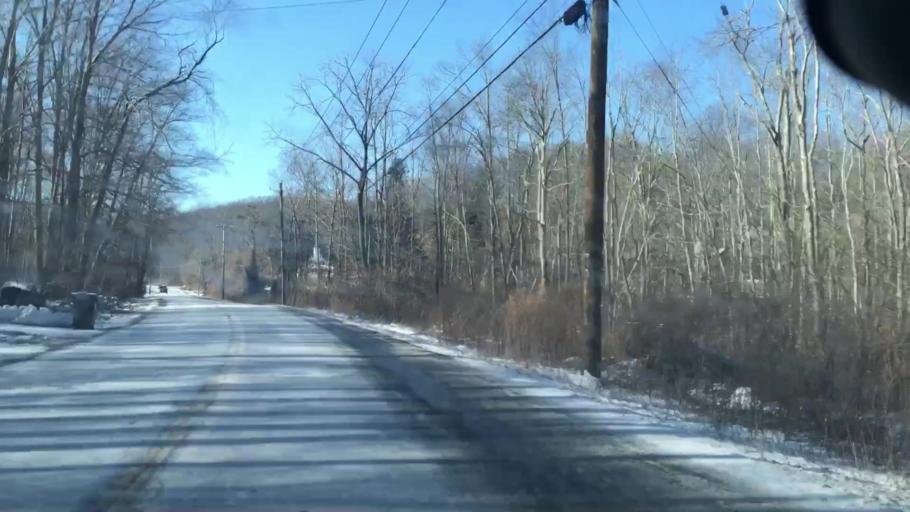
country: US
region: New York
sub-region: Putnam County
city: Carmel Hamlet
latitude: 41.3884
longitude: -73.6888
